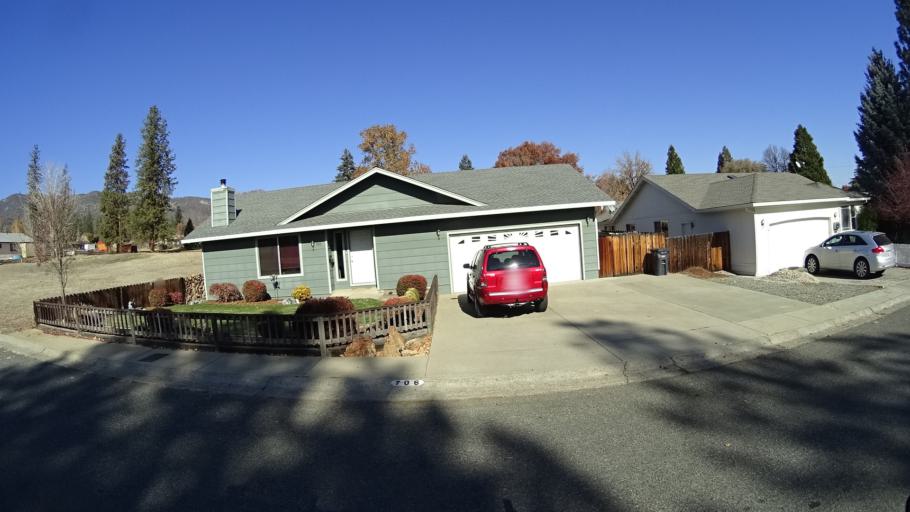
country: US
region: California
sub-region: Siskiyou County
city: Yreka
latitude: 41.7369
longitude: -122.6430
